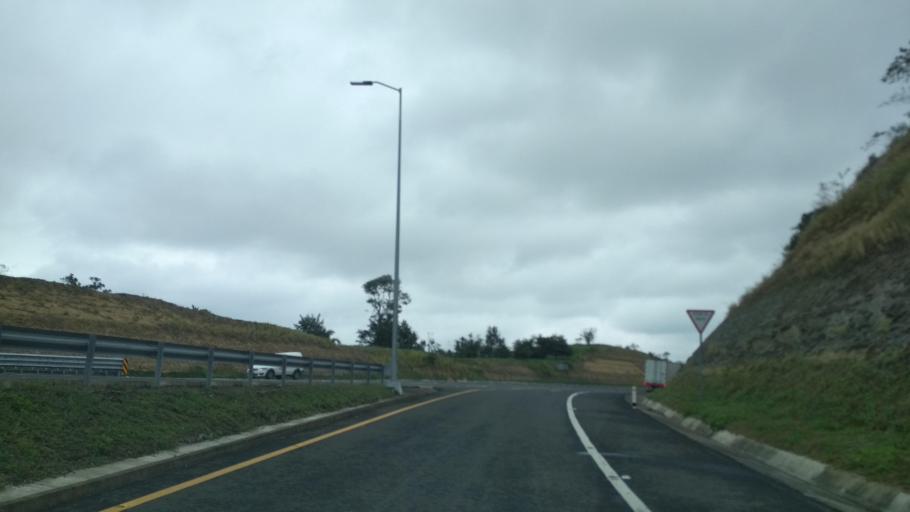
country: MX
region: Veracruz
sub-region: Papantla
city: Polutla
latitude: 20.4589
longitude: -97.2458
